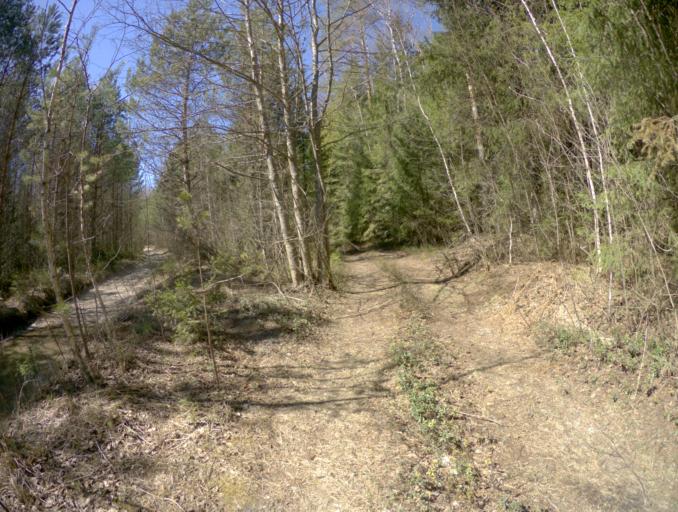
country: RU
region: Vladimir
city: Golovino
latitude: 55.8952
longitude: 40.4187
